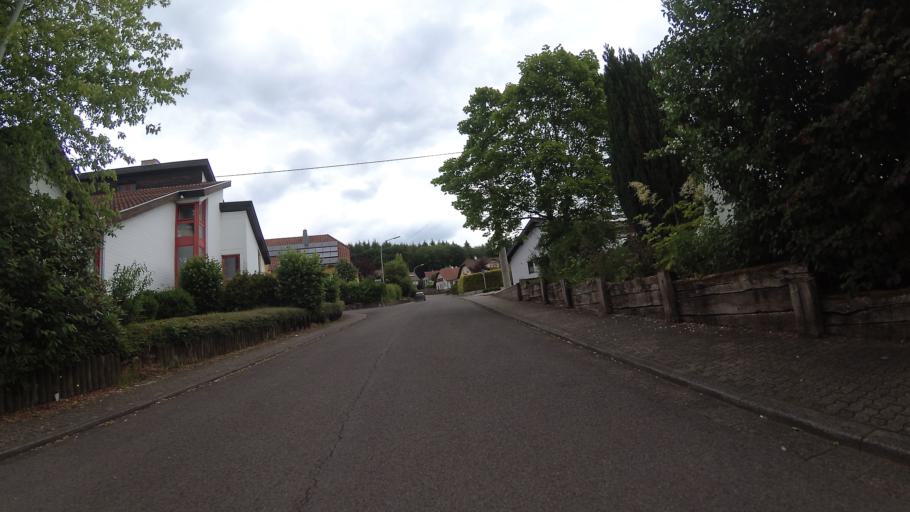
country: DE
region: Saarland
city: Schmelz
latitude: 49.3954
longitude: 6.8347
